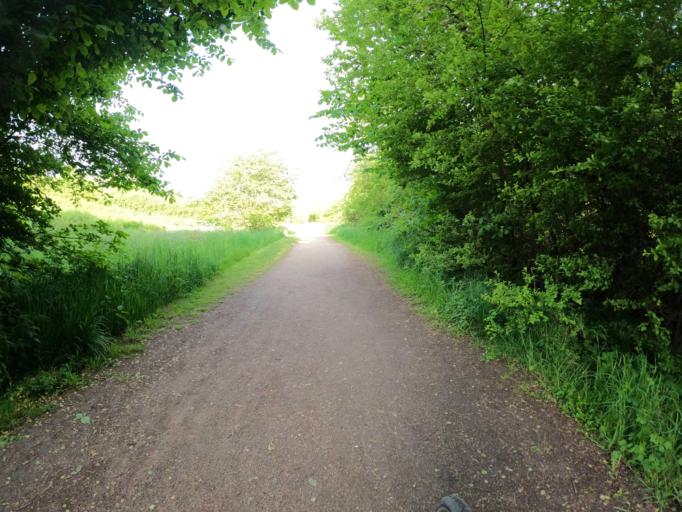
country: DK
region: Capital Region
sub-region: Ishoj Kommune
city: Ishoj
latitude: 55.6084
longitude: 12.3315
